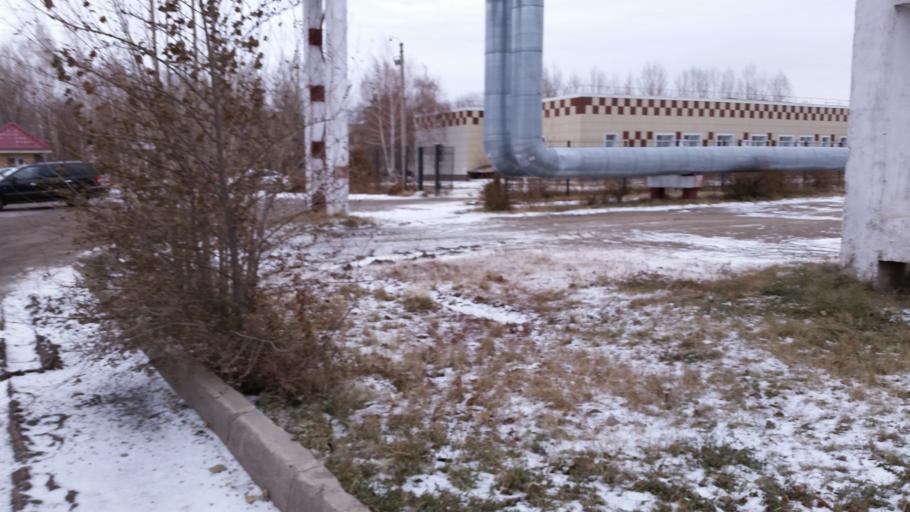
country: KZ
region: Astana Qalasy
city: Astana
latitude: 51.1635
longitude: 71.4846
